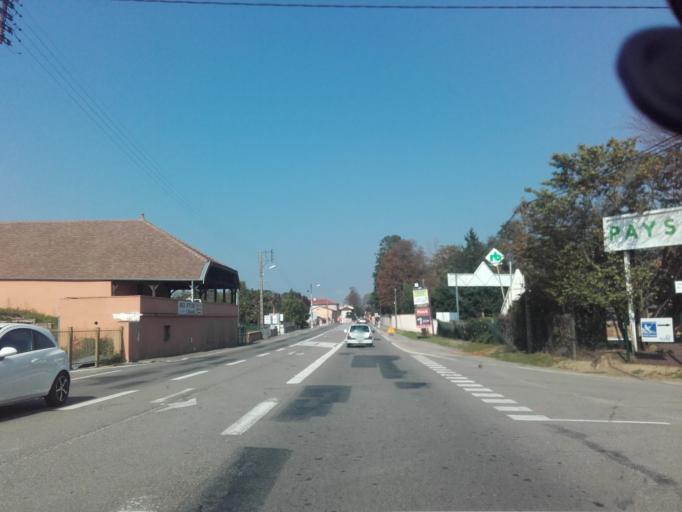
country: FR
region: Bourgogne
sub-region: Departement de Saone-et-Loire
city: Creches-sur-Saone
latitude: 46.2385
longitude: 4.7870
